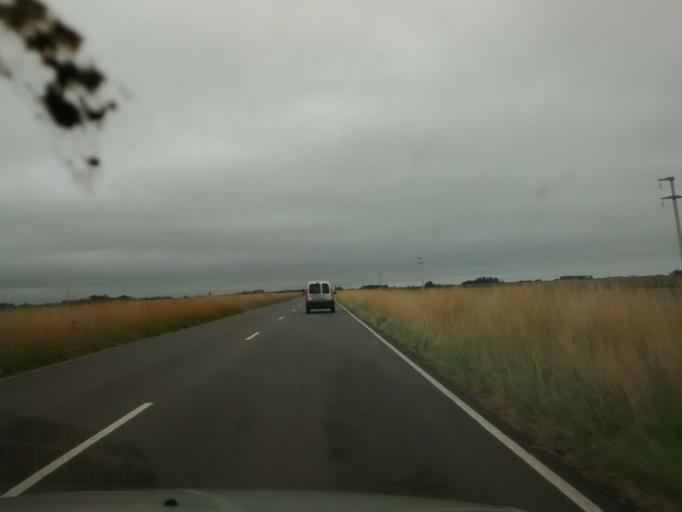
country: AR
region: Buenos Aires
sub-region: Partido de Ayacucho
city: Ayacucho
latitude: -37.0128
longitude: -58.5377
